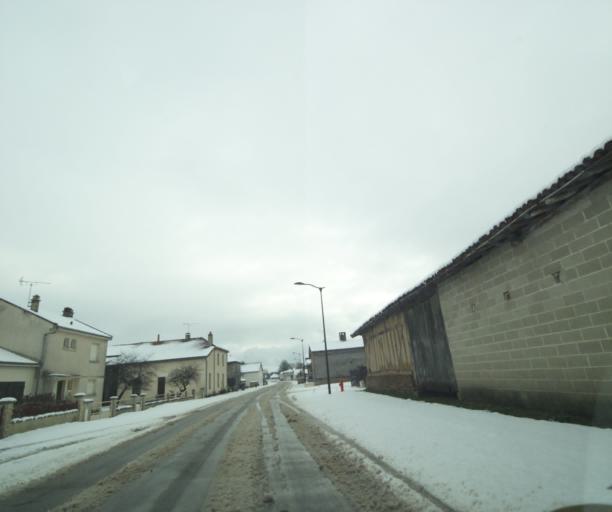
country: FR
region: Champagne-Ardenne
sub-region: Departement de la Haute-Marne
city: Montier-en-Der
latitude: 48.4363
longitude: 4.7149
